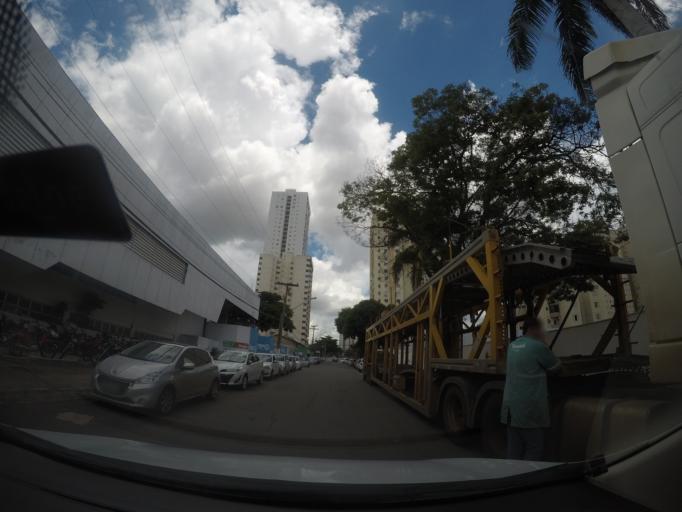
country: BR
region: Goias
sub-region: Goiania
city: Goiania
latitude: -16.6914
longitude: -49.2760
